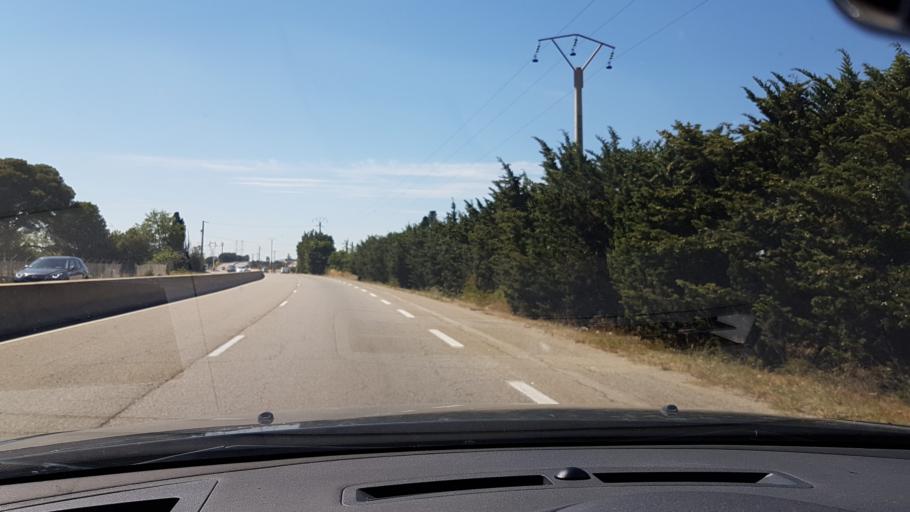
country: FR
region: Provence-Alpes-Cote d'Azur
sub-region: Departement des Bouches-du-Rhone
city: Fos-sur-Mer
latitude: 43.4693
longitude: 4.9113
